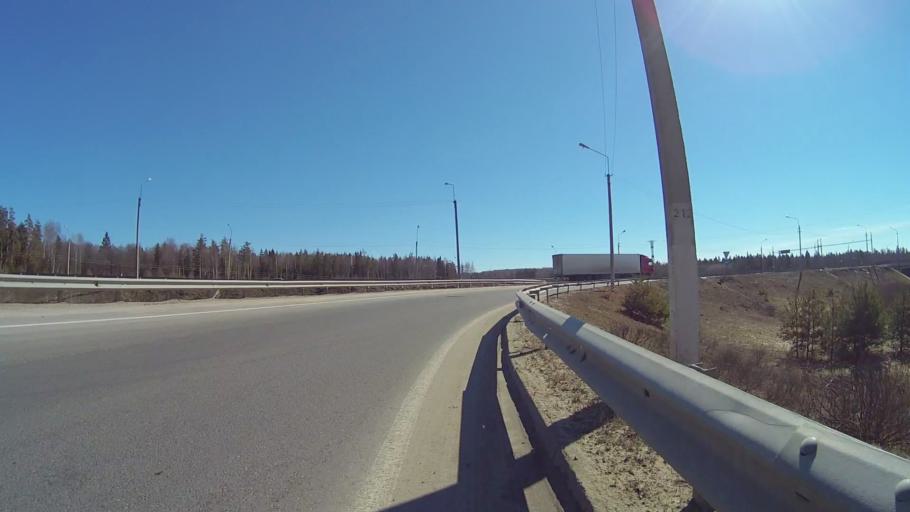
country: RU
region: Vladimir
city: Kommunar
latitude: 56.0814
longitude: 40.4749
